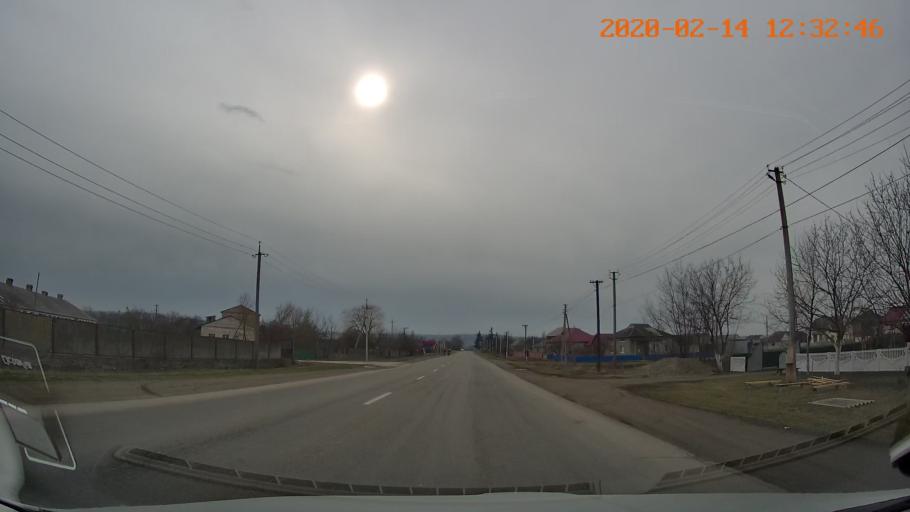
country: RO
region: Botosani
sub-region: Comuna Darabani
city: Bajura
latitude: 48.2399
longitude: 26.5477
